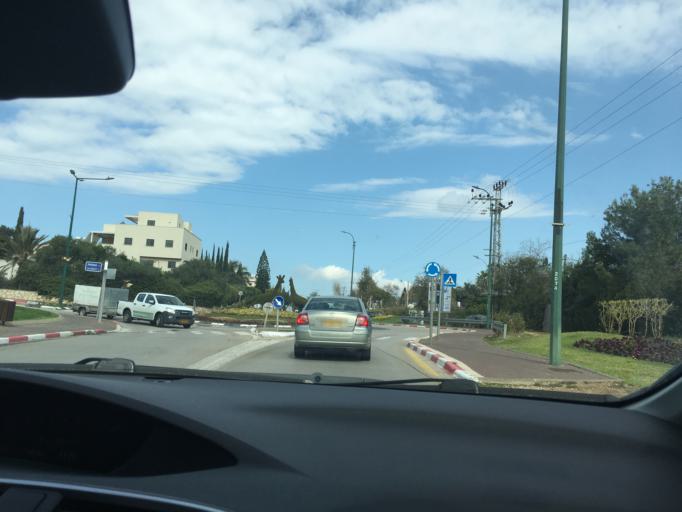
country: IL
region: Tel Aviv
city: Ramat HaSharon
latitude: 32.1653
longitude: 34.8530
